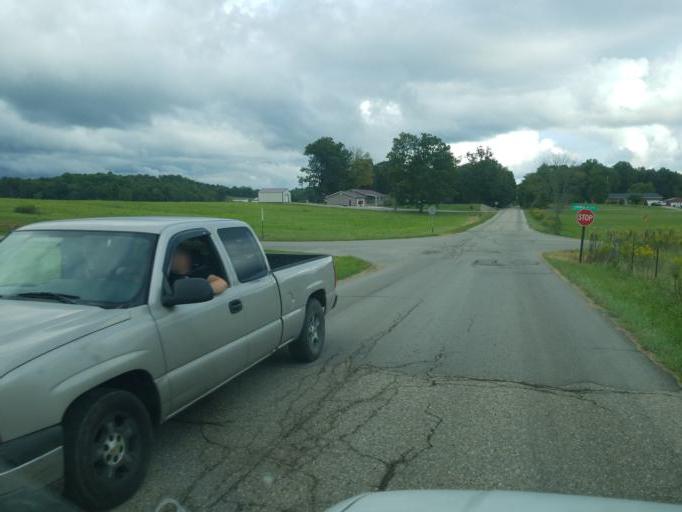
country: US
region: Ohio
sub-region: Jackson County
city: Oak Hill
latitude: 38.9427
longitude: -82.6034
